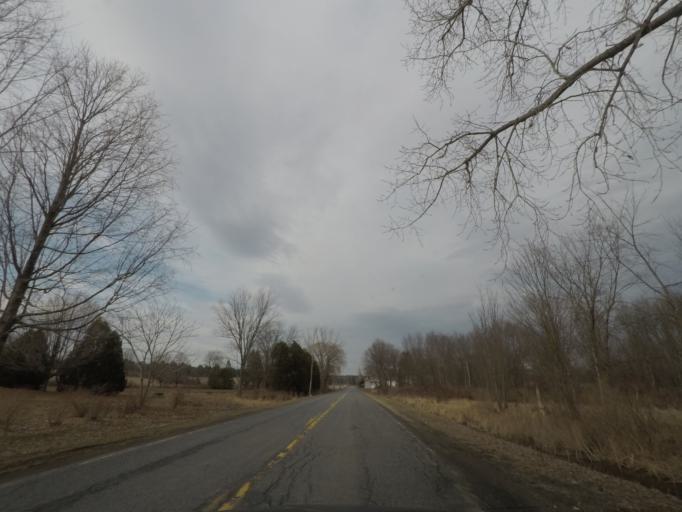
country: US
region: New York
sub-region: Washington County
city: Cambridge
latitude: 42.9628
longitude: -73.4776
